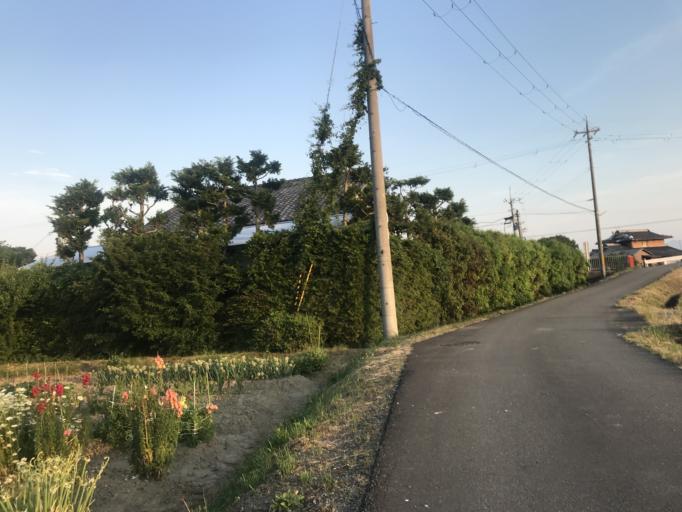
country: JP
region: Kyoto
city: Kameoka
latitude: 35.0526
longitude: 135.5532
